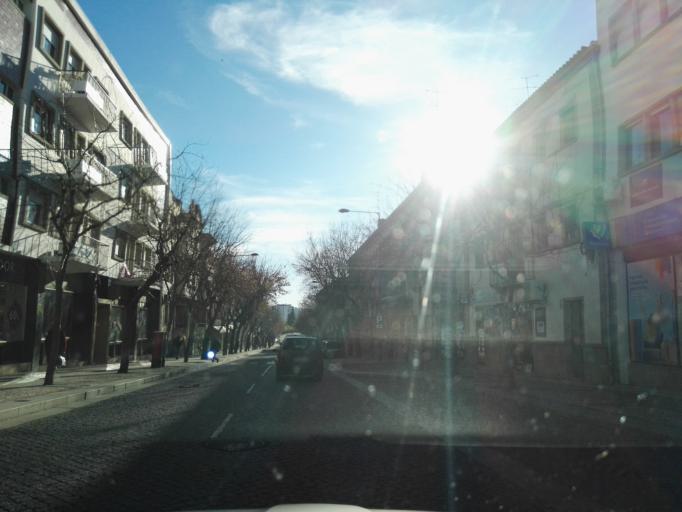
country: PT
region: Castelo Branco
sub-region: Castelo Branco
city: Castelo Branco
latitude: 39.8213
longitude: -7.4948
